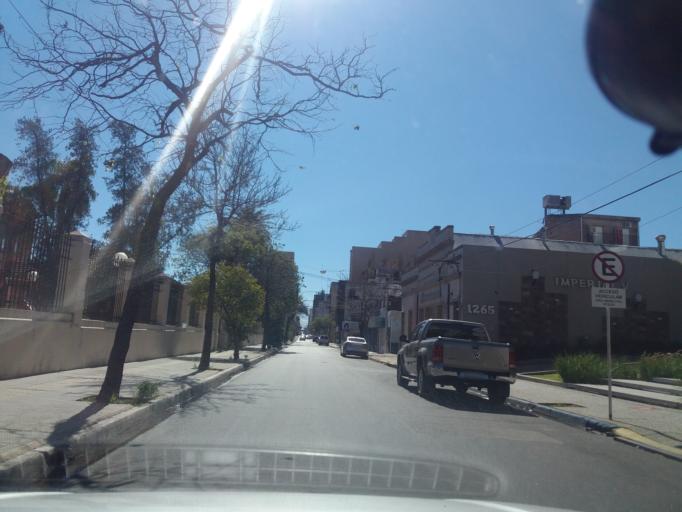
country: AR
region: Corrientes
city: Corrientes
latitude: -27.4717
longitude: -58.8360
